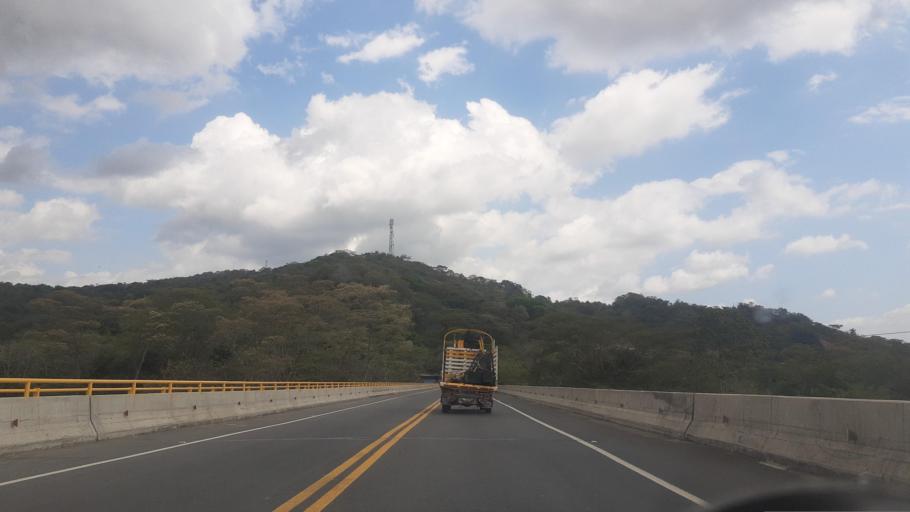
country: CO
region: Casanare
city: Tauramena
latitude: 5.0107
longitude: -72.6869
